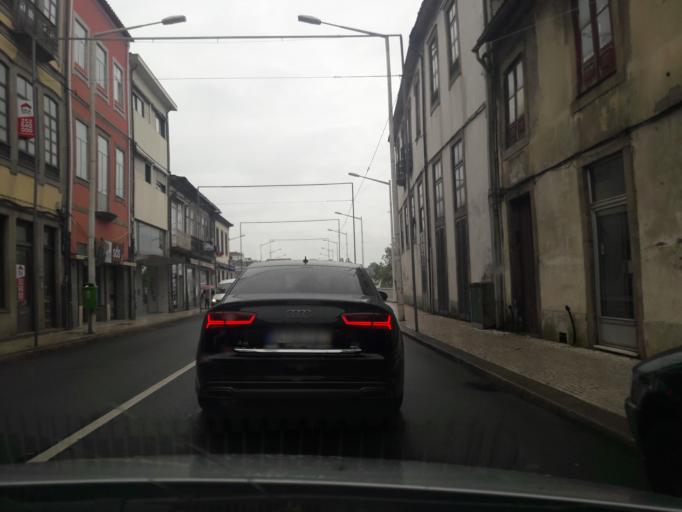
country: PT
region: Porto
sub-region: Vila do Conde
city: Vila do Conde
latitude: 41.3525
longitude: -8.7401
